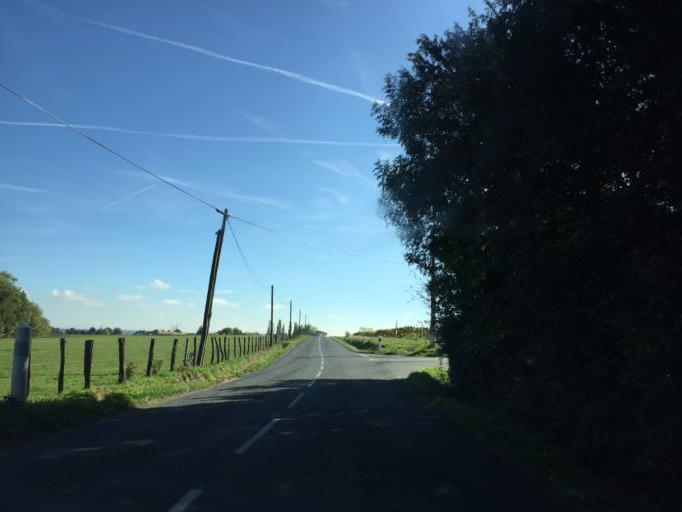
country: FR
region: Rhone-Alpes
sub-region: Departement du Rhone
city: Charentay
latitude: 46.0727
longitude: 4.6843
